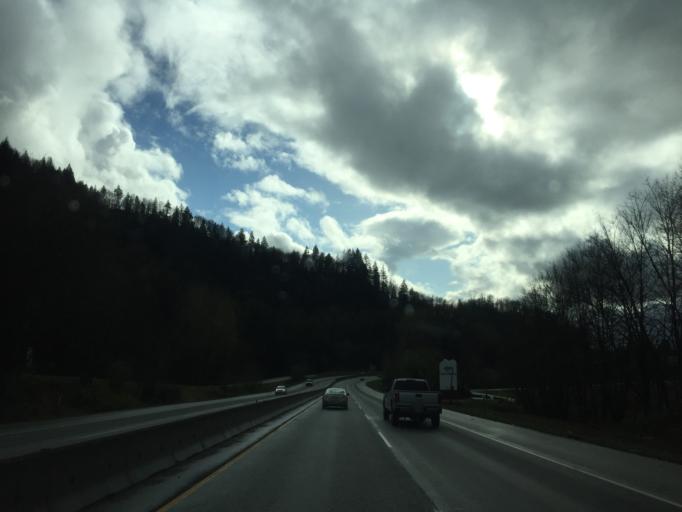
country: CA
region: British Columbia
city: Agassiz
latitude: 49.1625
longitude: -121.7953
